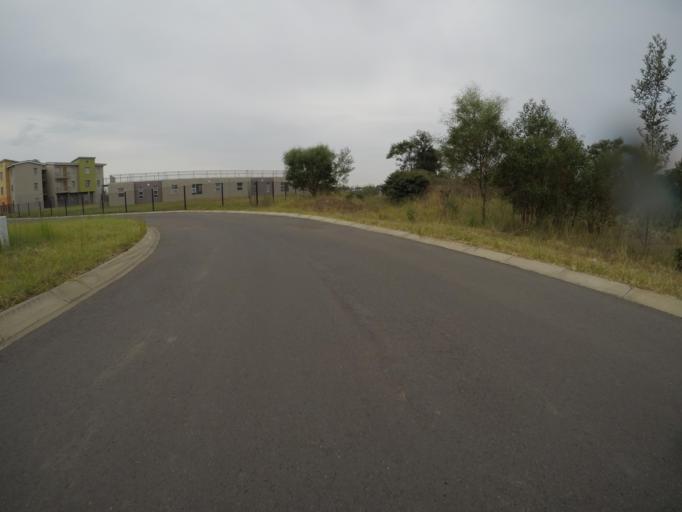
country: ZA
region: Eastern Cape
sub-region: Buffalo City Metropolitan Municipality
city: East London
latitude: -32.9958
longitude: 27.8544
